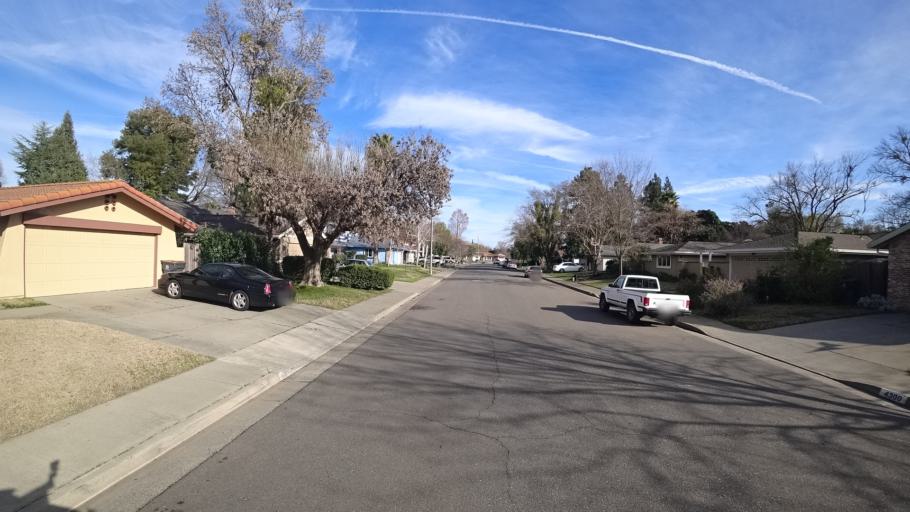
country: US
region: California
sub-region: Yolo County
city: Davis
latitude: 38.5471
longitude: -121.6993
